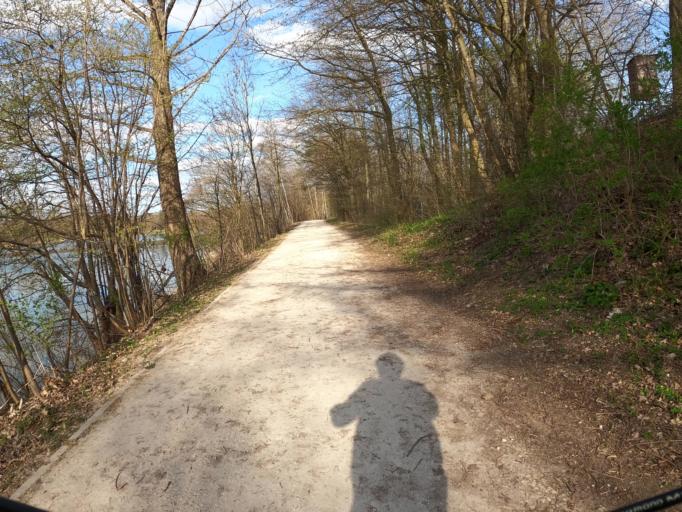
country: DE
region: Bavaria
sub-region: Swabia
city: Neu-Ulm
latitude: 48.4265
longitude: 10.0401
